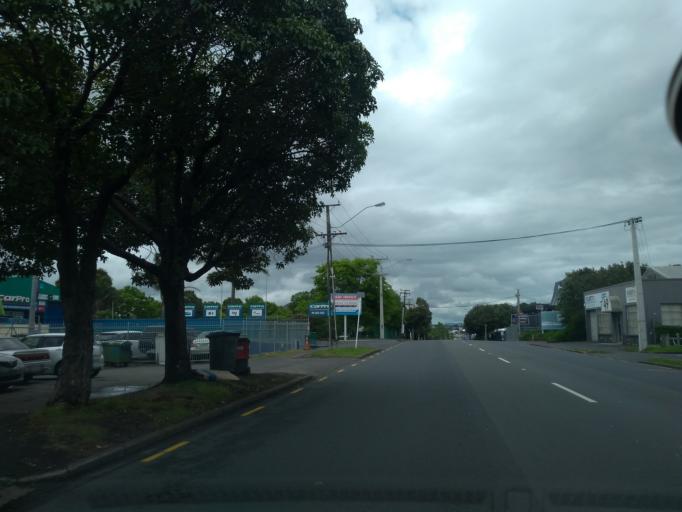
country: NZ
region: Auckland
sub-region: Auckland
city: Tamaki
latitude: -36.9156
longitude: 174.8168
